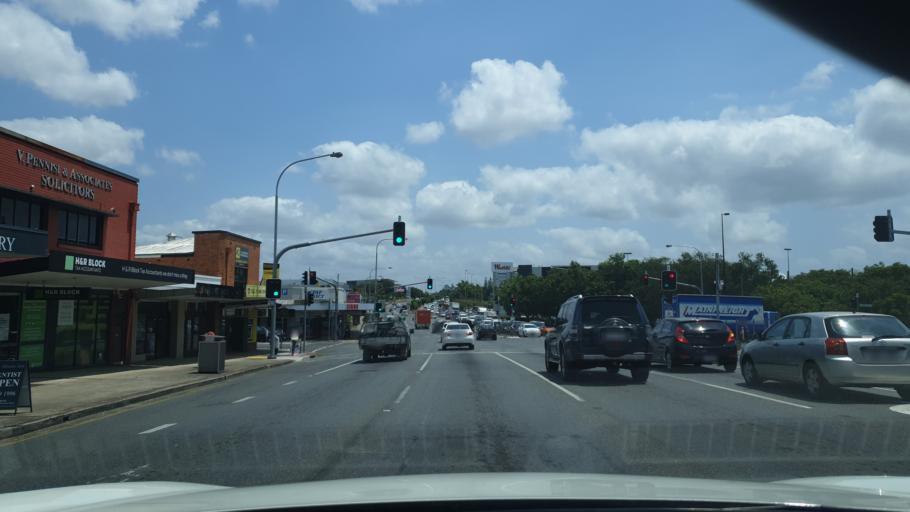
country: AU
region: Queensland
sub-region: Brisbane
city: Chermside West
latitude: -27.3864
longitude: 153.0309
